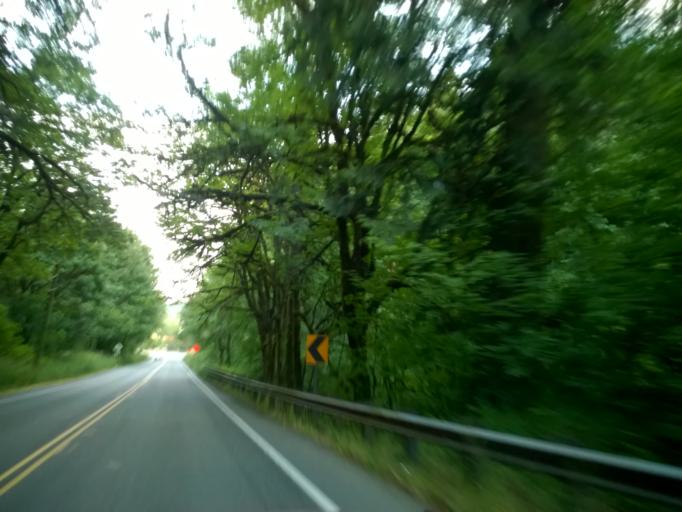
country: US
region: Washington
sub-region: King County
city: Duvall
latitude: 47.7442
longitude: -122.0108
